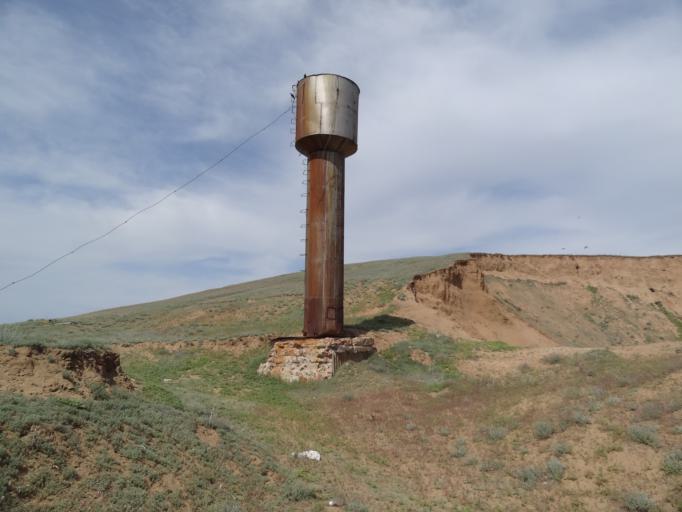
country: RU
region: Saratov
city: Privolzhskiy
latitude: 51.2047
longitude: 45.9205
